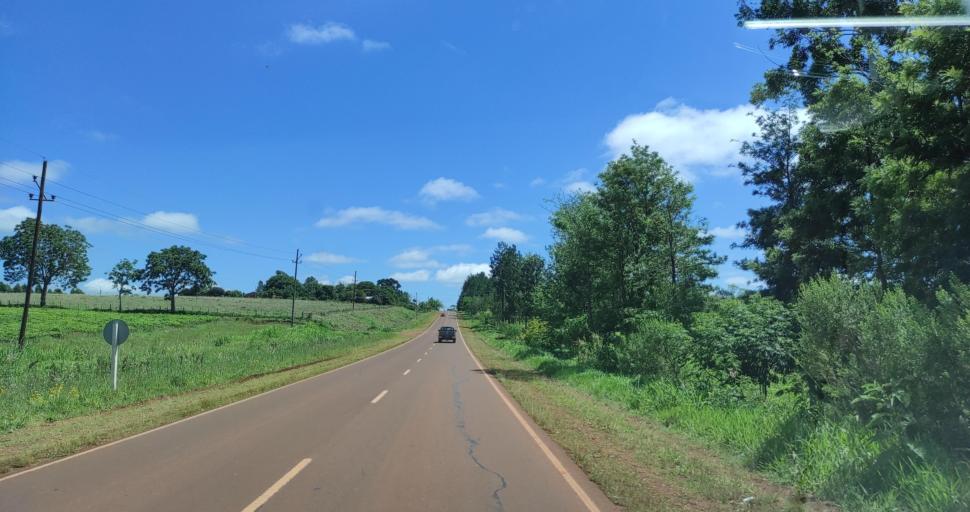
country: AR
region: Misiones
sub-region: Departamento de Veinticinco de Mayo
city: Veinticinco de Mayo
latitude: -27.4020
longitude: -54.7502
